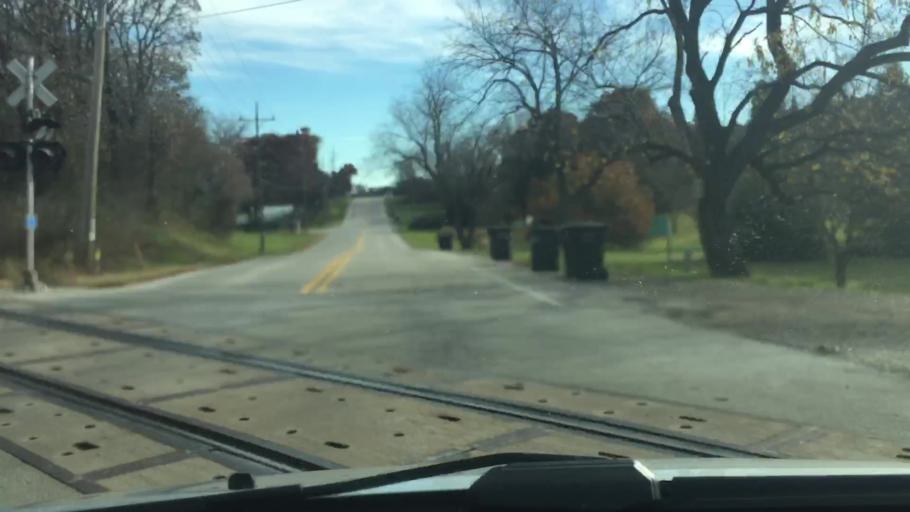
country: US
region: Wisconsin
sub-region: Waukesha County
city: North Prairie
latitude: 42.9448
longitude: -88.3872
